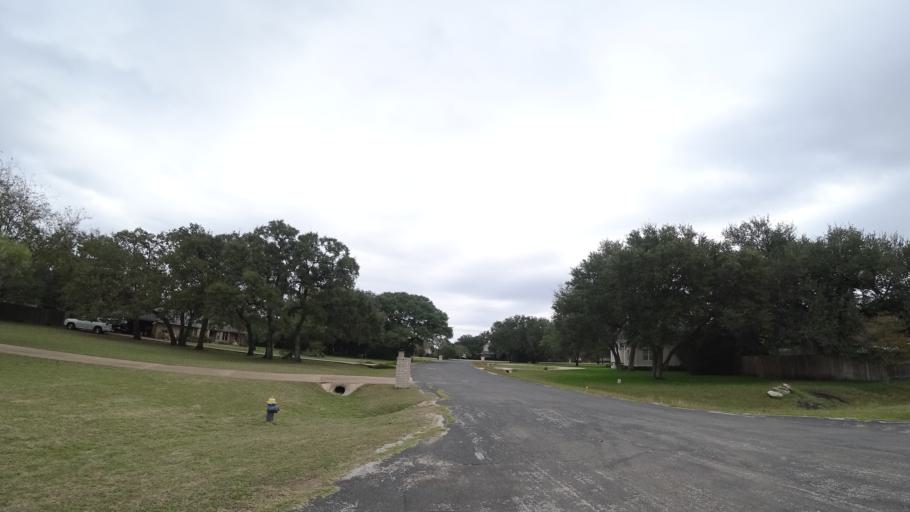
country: US
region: Texas
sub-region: Travis County
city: Shady Hollow
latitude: 30.1547
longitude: -97.8645
